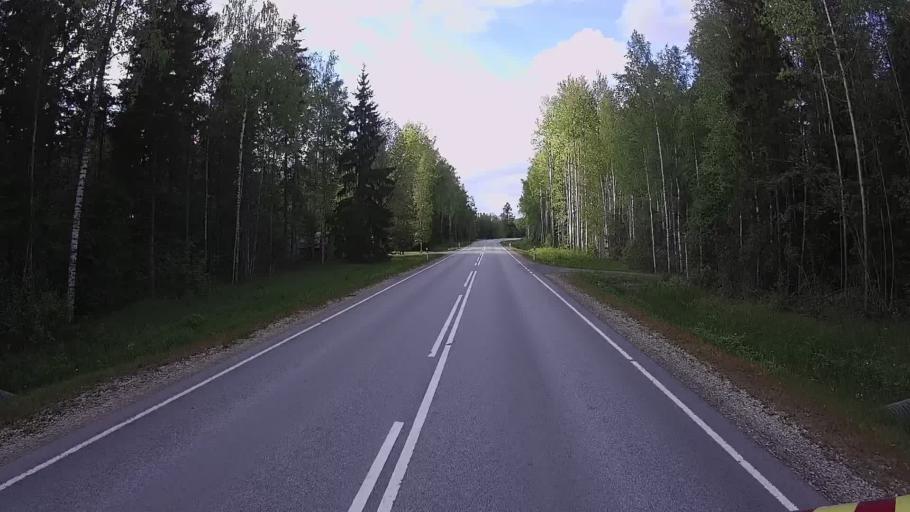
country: EE
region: Jogevamaa
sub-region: Mustvee linn
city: Mustvee
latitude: 58.9727
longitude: 26.8276
